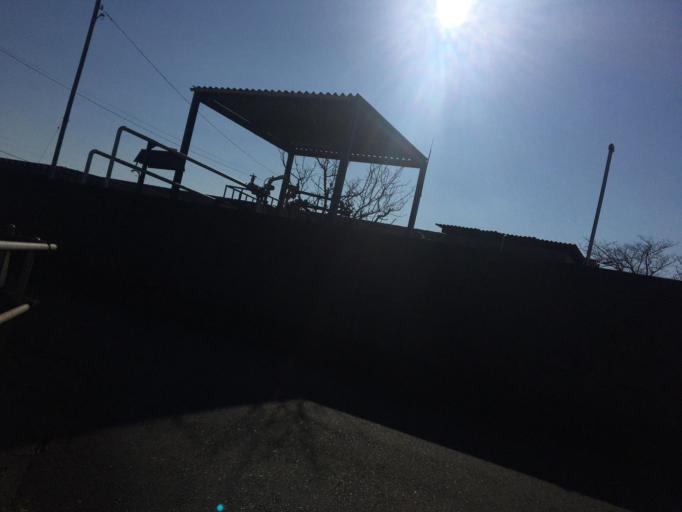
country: JP
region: Saitama
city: Soka
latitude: 35.8011
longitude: 139.8210
